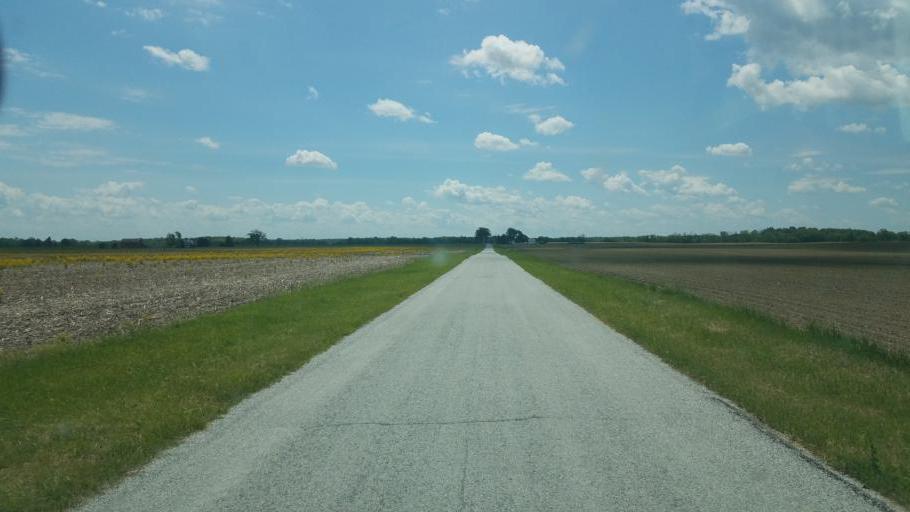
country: US
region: Ohio
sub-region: Hardin County
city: Forest
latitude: 40.6780
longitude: -83.4598
